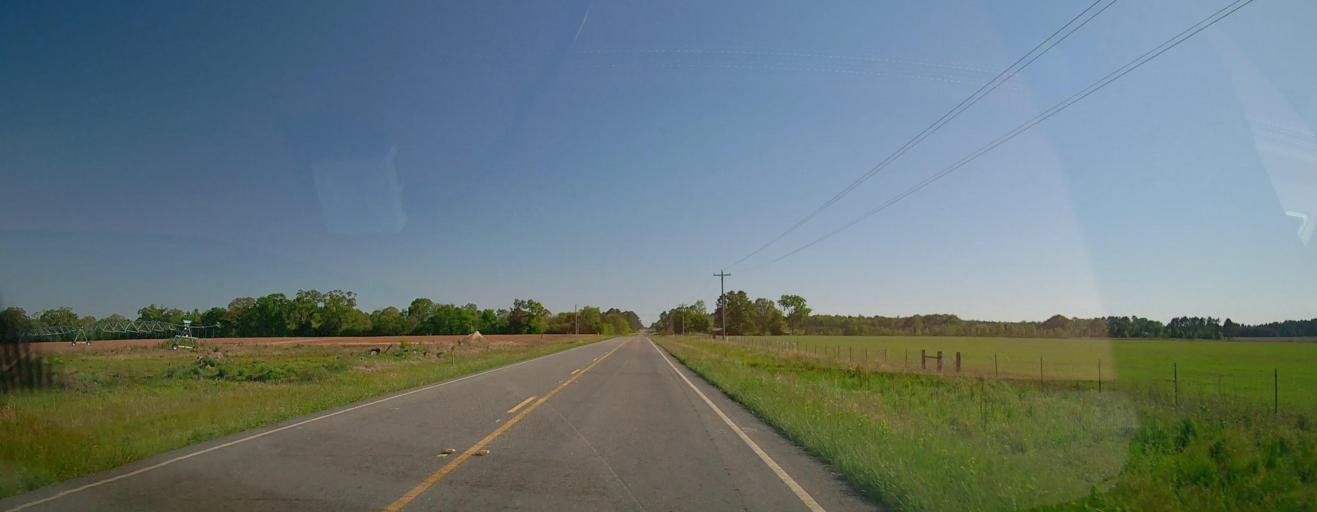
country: US
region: Georgia
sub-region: Wilcox County
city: Rochelle
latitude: 32.0717
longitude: -83.5035
